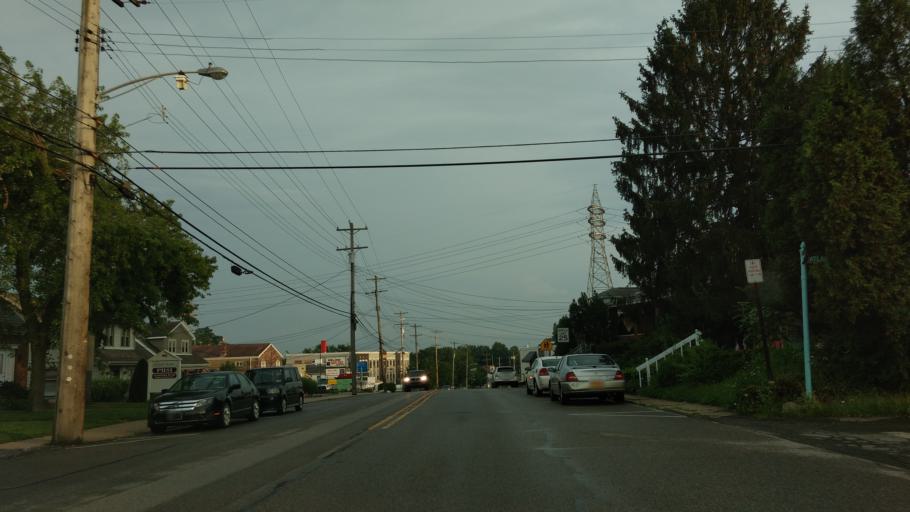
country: US
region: Pennsylvania
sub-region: Allegheny County
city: West View
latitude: 40.5377
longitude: -80.0363
